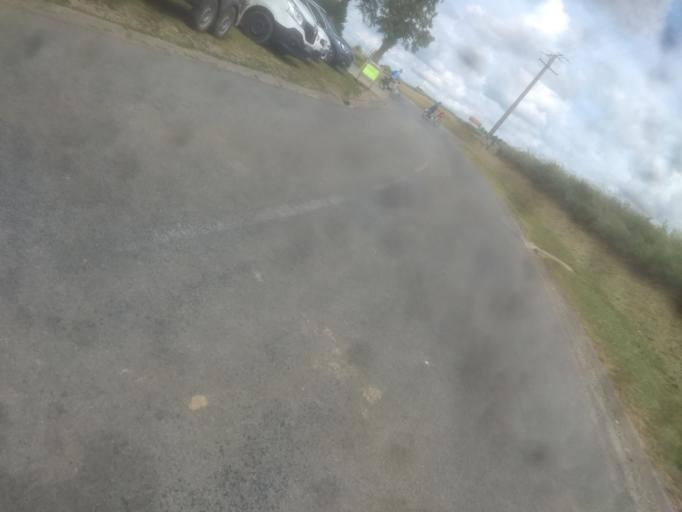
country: FR
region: Nord-Pas-de-Calais
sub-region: Departement du Pas-de-Calais
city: Duisans
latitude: 50.3072
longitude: 2.6644
